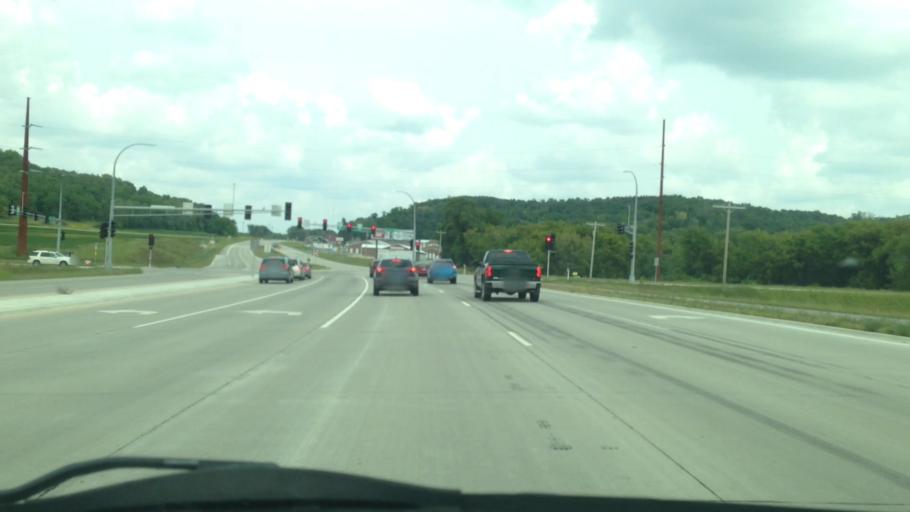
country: US
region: Minnesota
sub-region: Olmsted County
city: Rochester
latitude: 44.0711
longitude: -92.4486
